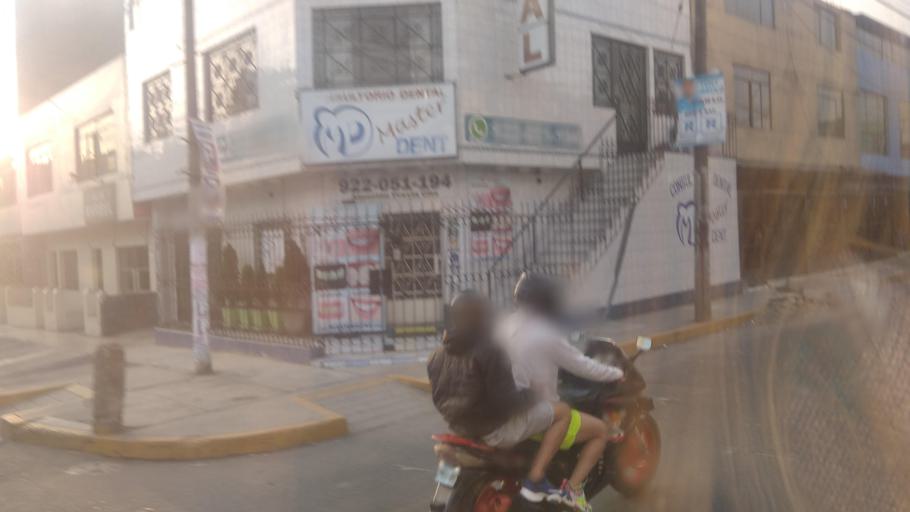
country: PE
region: Lima
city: Lima
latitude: -12.0251
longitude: -77.0005
